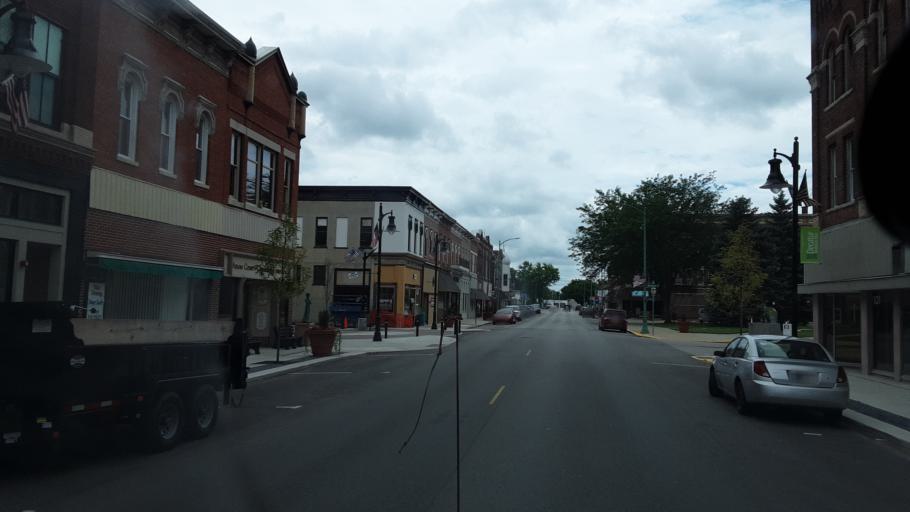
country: US
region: Indiana
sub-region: Adams County
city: Decatur
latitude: 40.8304
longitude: -84.9241
